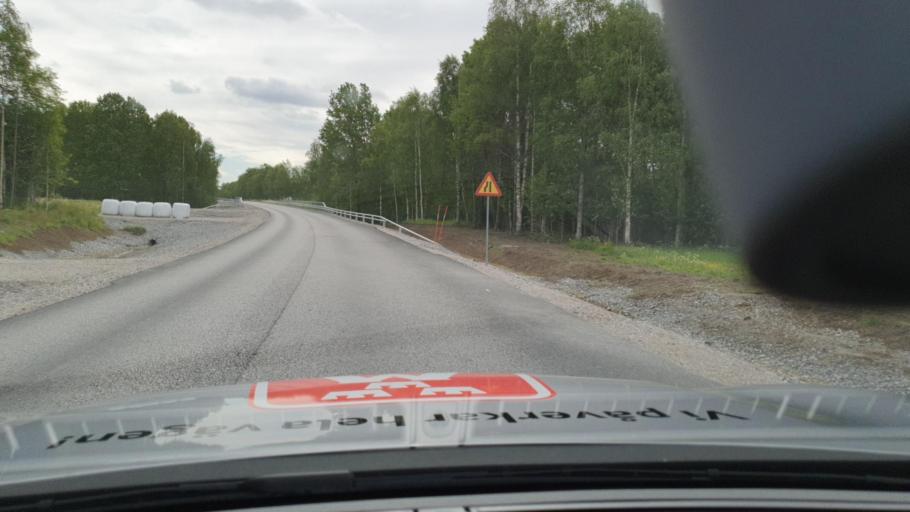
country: SE
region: Norrbotten
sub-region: Kalix Kommun
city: Rolfs
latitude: 65.8818
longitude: 23.0688
